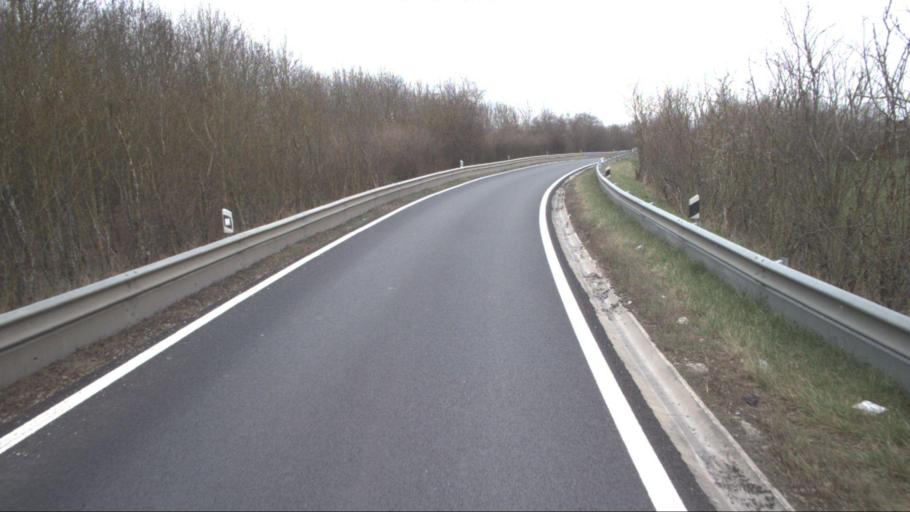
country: FR
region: Ile-de-France
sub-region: Departement des Yvelines
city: Ablis
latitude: 48.5152
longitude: 1.8262
